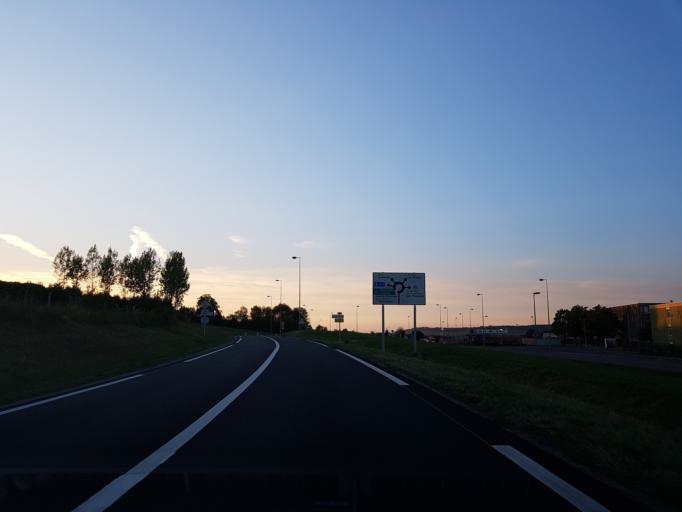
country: FR
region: Champagne-Ardenne
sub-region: Departement de la Haute-Marne
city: Langres
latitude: 47.8686
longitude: 5.3417
